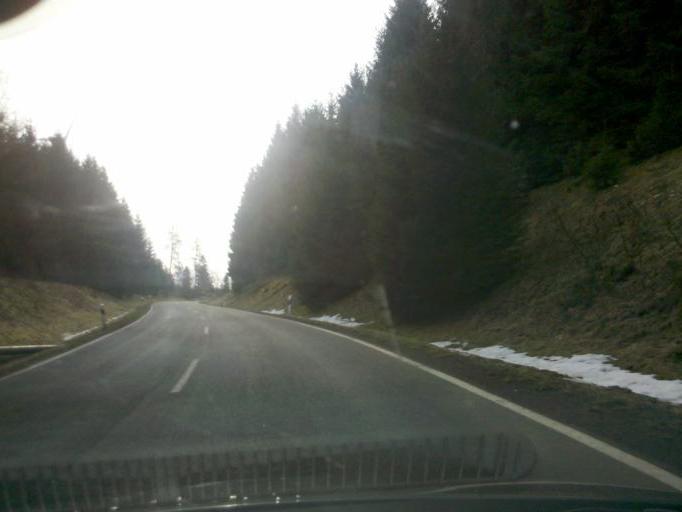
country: DE
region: Hesse
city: Dillenburg
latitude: 50.7933
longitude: 8.2681
